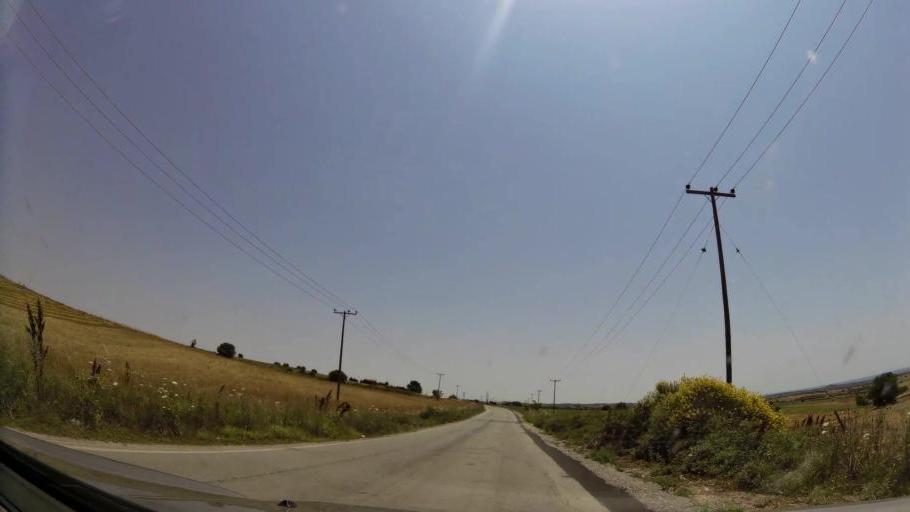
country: GR
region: Central Macedonia
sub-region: Nomos Thessalonikis
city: Neoi Epivates
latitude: 40.4652
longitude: 22.9036
